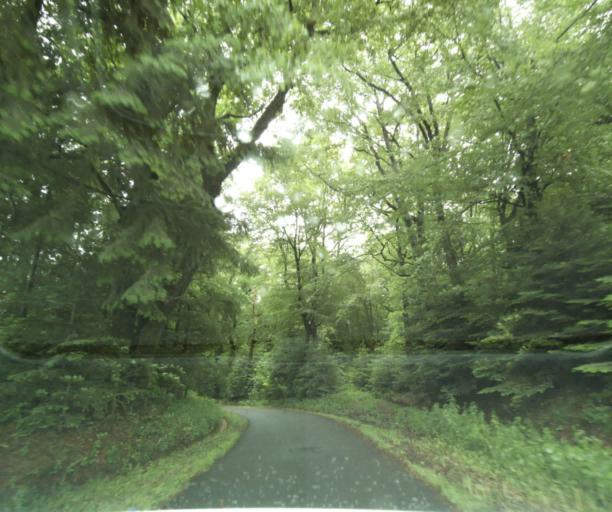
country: FR
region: Bourgogne
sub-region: Departement de Saone-et-Loire
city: Saint-Vallier
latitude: 46.4891
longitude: 4.4480
